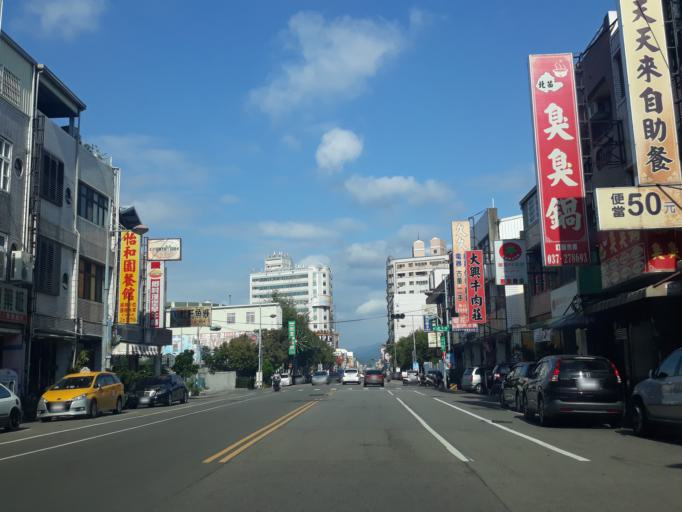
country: TW
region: Taiwan
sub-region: Miaoli
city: Miaoli
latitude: 24.5709
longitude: 120.8277
